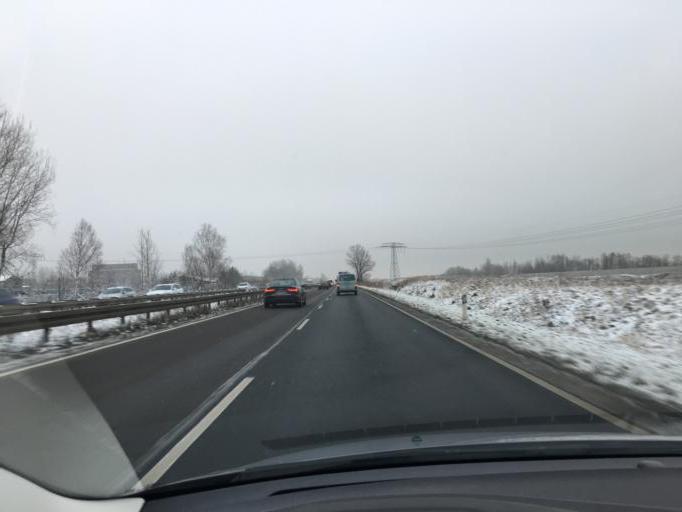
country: DE
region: Saxony
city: Espenhain
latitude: 51.1794
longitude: 12.4845
